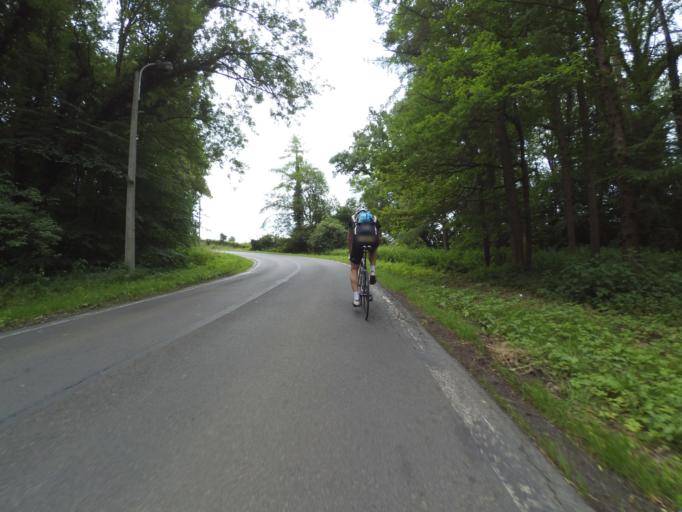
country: BE
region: Wallonia
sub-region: Province de Liege
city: La Calamine
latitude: 50.7026
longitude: 6.0351
